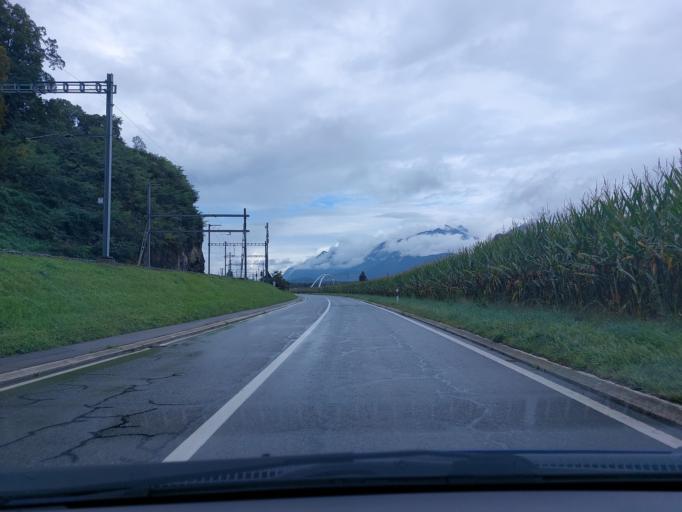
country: CH
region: Valais
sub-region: Saint-Maurice District
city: Saint-Maurice
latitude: 46.2277
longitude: 7.0013
